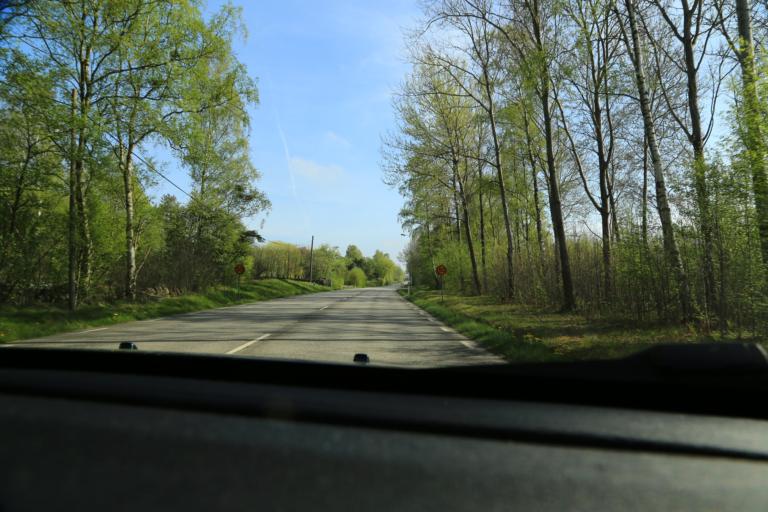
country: SE
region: Halland
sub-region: Varbergs Kommun
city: Varberg
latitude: 57.1775
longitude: 12.2277
